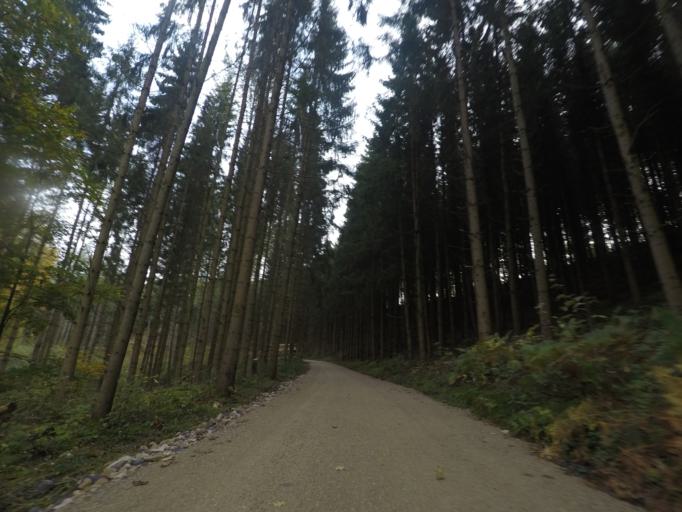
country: LU
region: Luxembourg
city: Itzig
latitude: 49.6069
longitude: 6.1873
